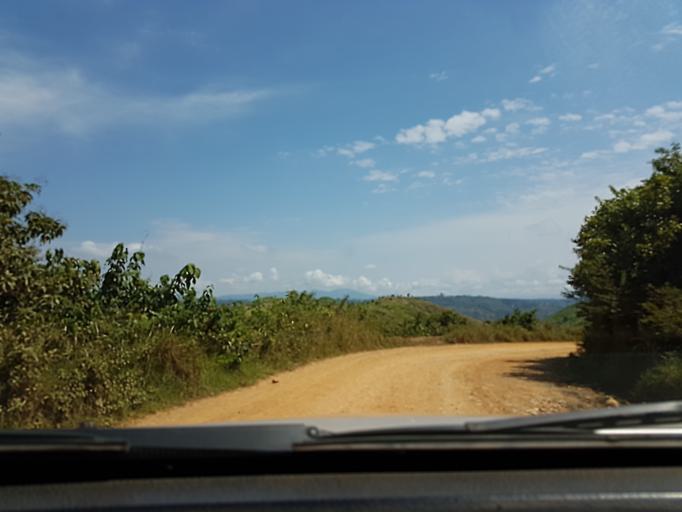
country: RW
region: Western Province
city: Cyangugu
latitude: -2.7031
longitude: 28.9110
